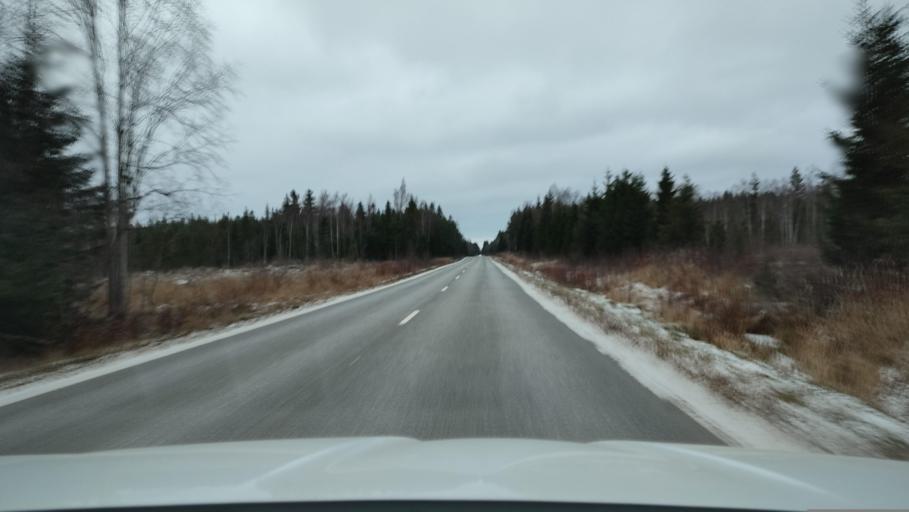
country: FI
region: Ostrobothnia
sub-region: Vaasa
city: Replot
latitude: 63.2577
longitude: 21.3660
